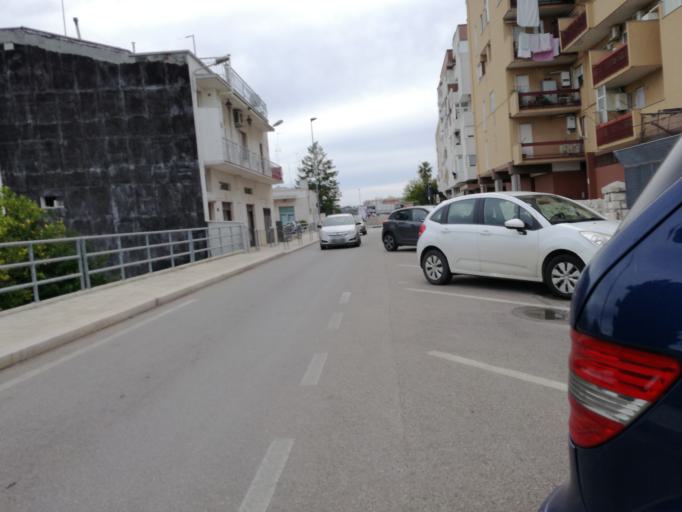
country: IT
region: Apulia
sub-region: Provincia di Bari
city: Adelfia
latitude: 41.0044
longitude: 16.8720
